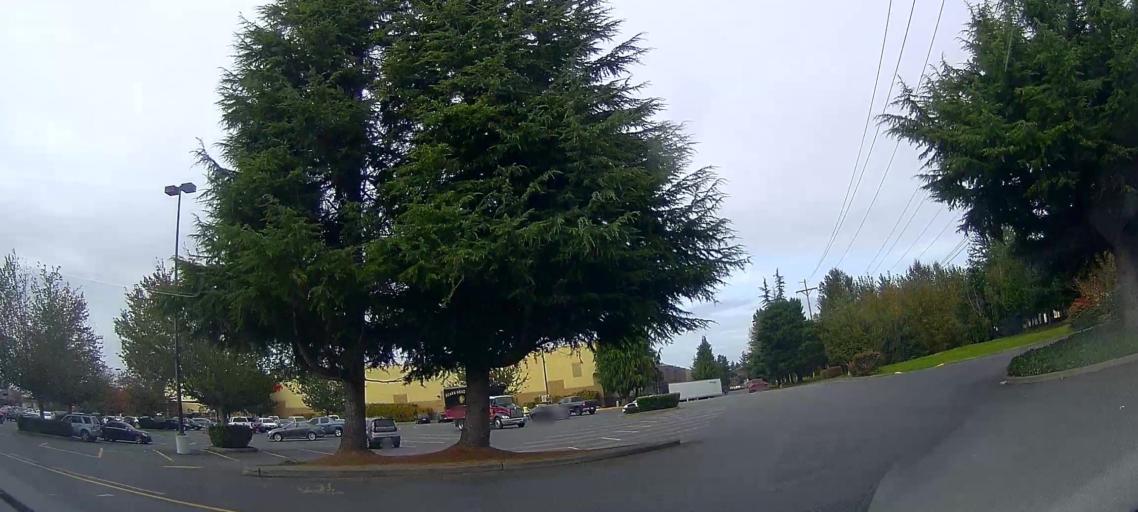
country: US
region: Washington
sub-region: Skagit County
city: Burlington
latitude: 48.4652
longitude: -122.3325
